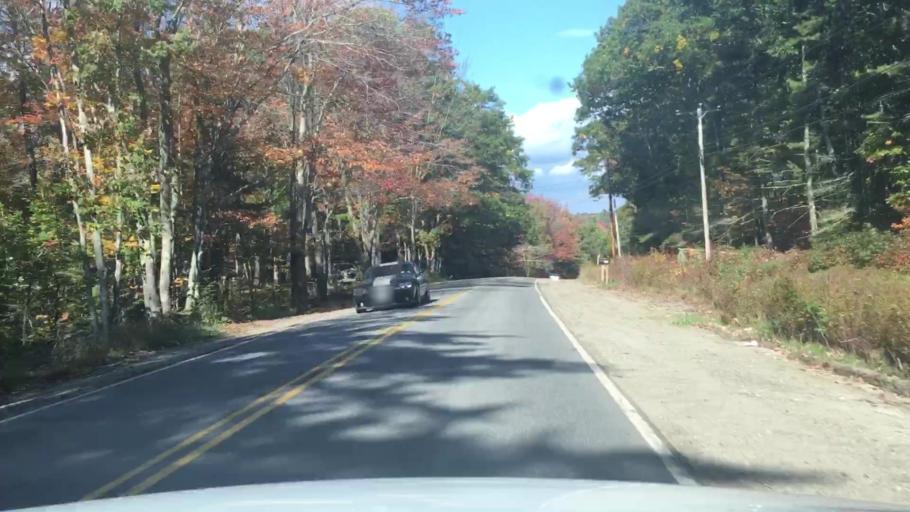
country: US
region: Maine
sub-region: Knox County
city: Warren
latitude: 44.1329
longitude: -69.2384
